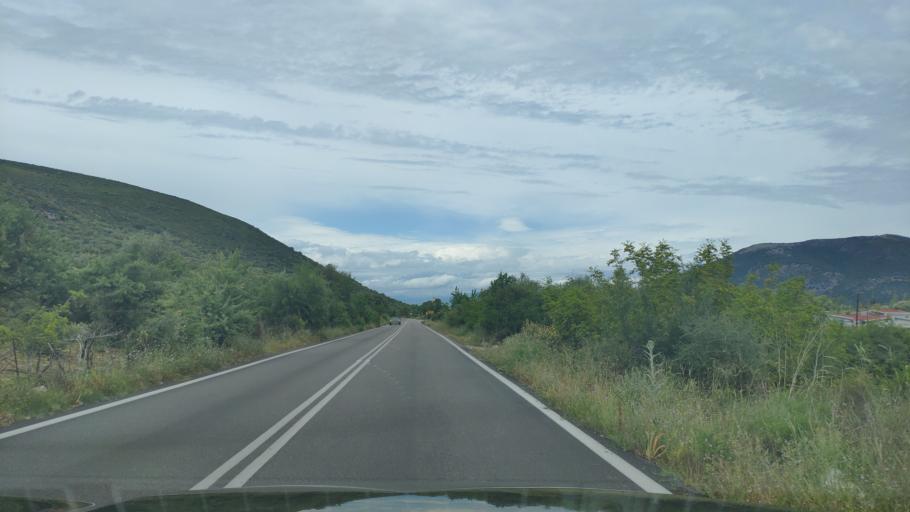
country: GR
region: West Greece
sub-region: Nomos Aitolias kai Akarnanias
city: Vonitsa
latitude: 38.8820
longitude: 20.8968
